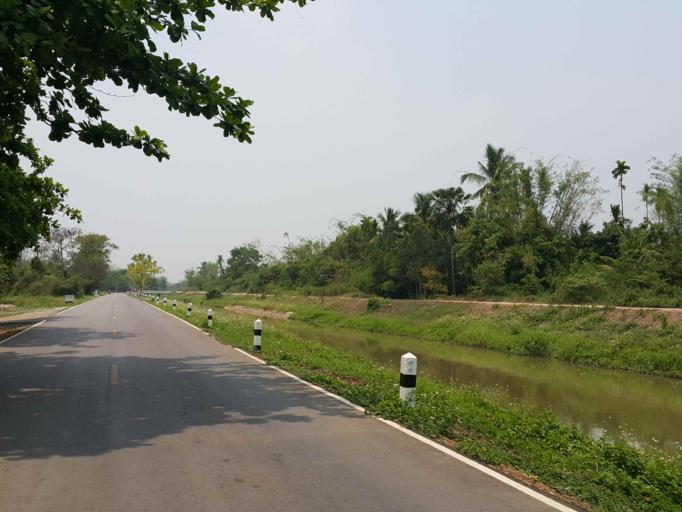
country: TH
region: Chiang Mai
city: San Sai
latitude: 18.8934
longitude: 99.0669
